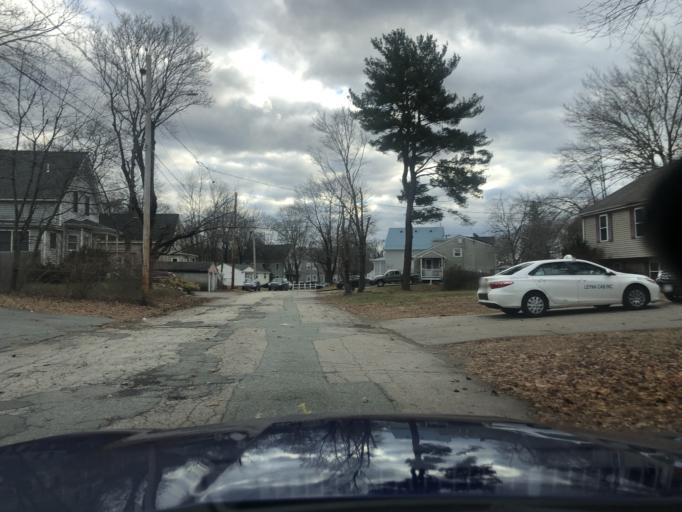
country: US
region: Massachusetts
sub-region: Plymouth County
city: Brockton
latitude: 42.1125
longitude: -71.0184
